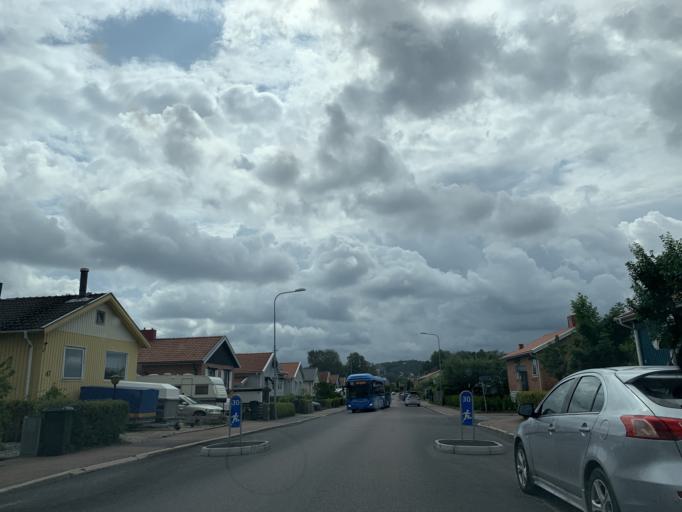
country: SE
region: Vaestra Goetaland
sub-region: Goteborg
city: Eriksbo
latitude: 57.7403
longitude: 12.0582
